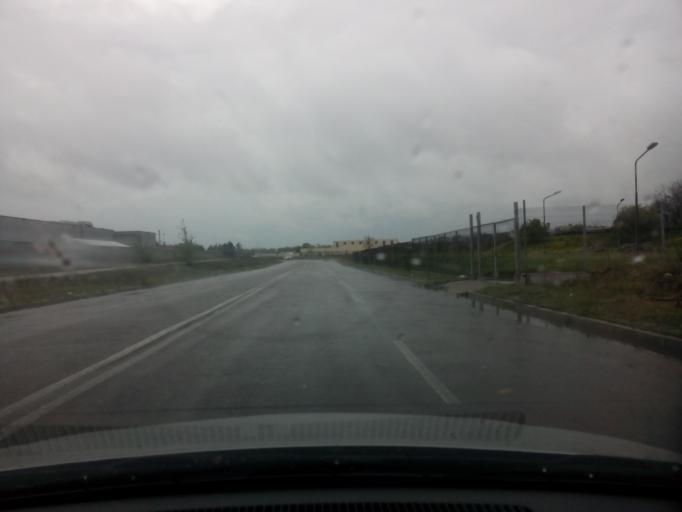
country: RO
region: Ilfov
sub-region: Comuna Otopeni
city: Otopeni
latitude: 44.5096
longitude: 26.0906
